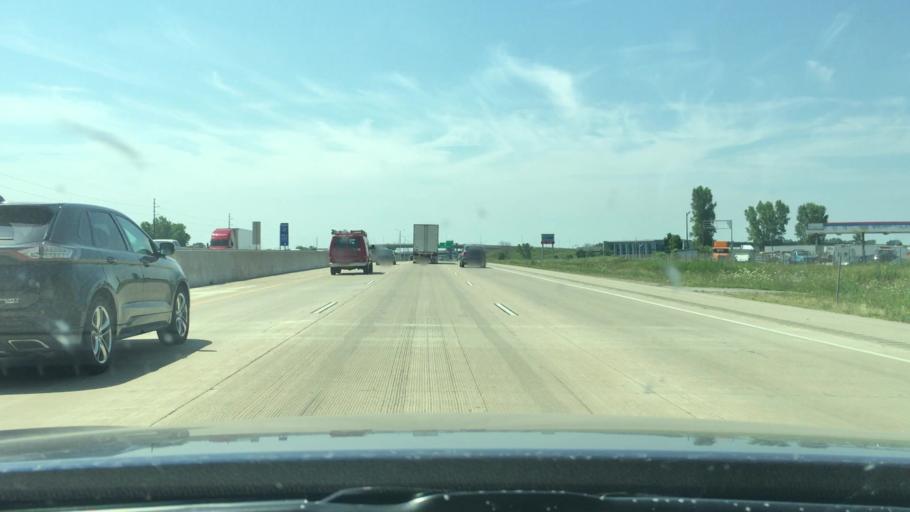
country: US
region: Wisconsin
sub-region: Winnebago County
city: Oshkosh
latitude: 44.0680
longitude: -88.5693
